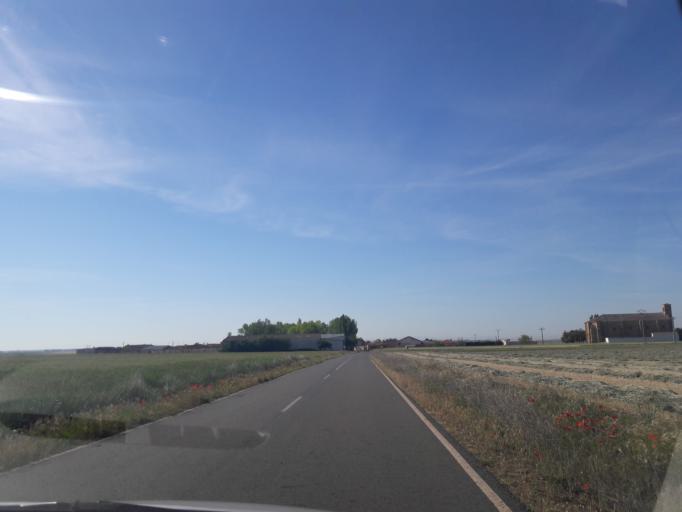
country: ES
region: Castille and Leon
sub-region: Provincia de Salamanca
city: Arcediano
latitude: 41.0971
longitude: -5.5635
